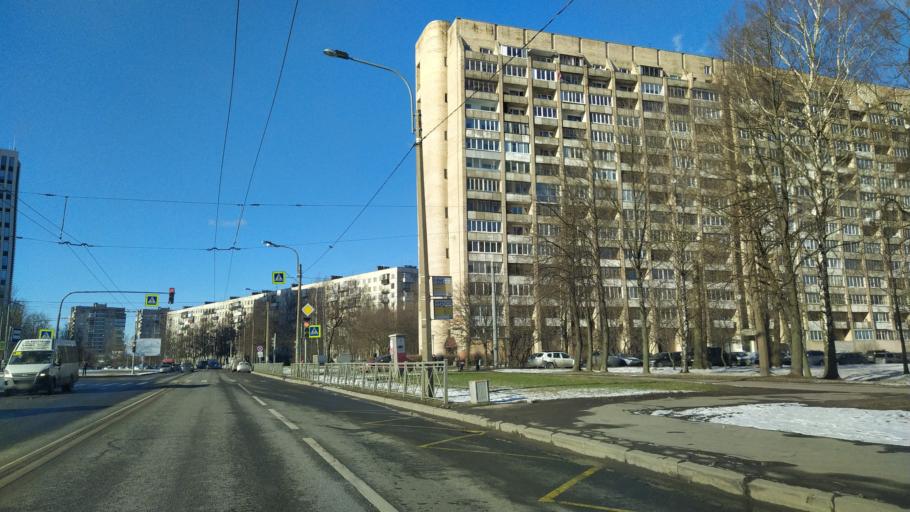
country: RU
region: Leningrad
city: Kalininskiy
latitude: 59.9703
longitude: 30.4239
